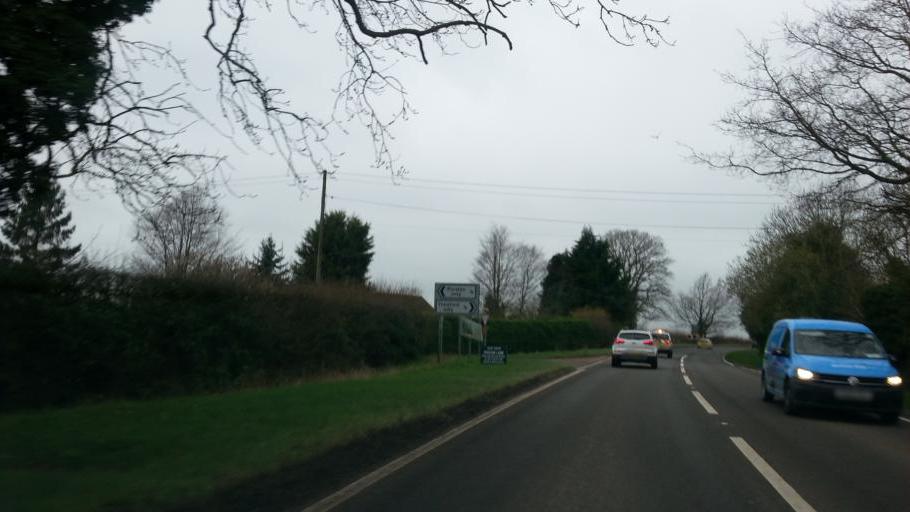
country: GB
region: England
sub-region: Oxfordshire
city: Adderbury
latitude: 52.0612
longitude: -1.2444
